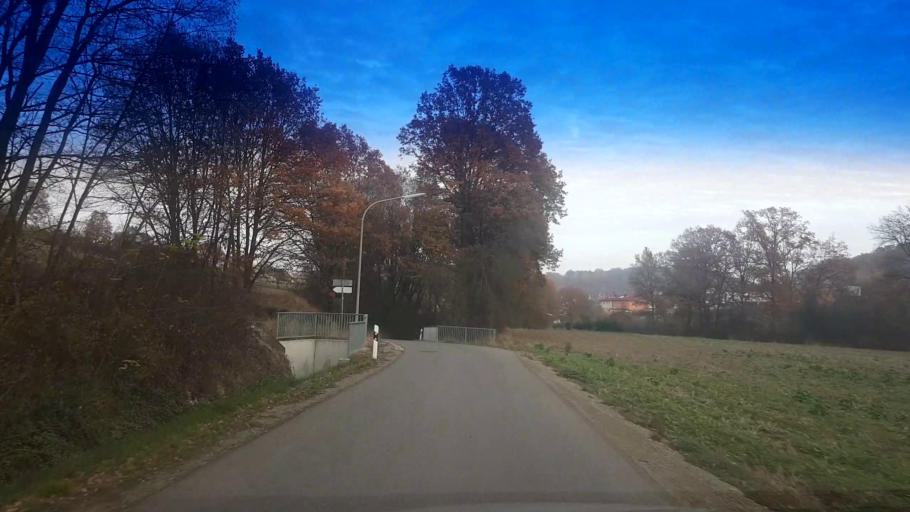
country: DE
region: Bavaria
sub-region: Upper Franconia
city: Viereth-Trunstadt
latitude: 49.9191
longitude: 10.7655
